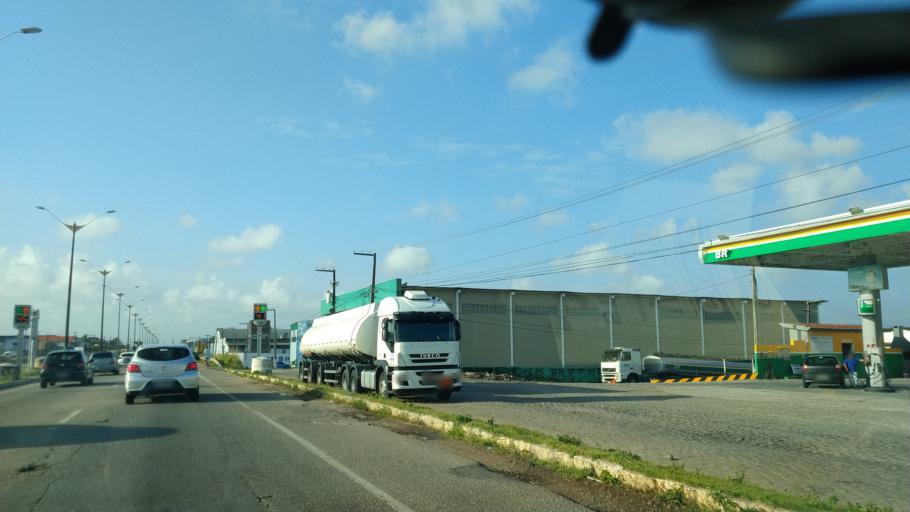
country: BR
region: Rio Grande do Norte
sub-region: Parnamirim
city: Parnamirim
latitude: -5.9023
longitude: -35.2595
